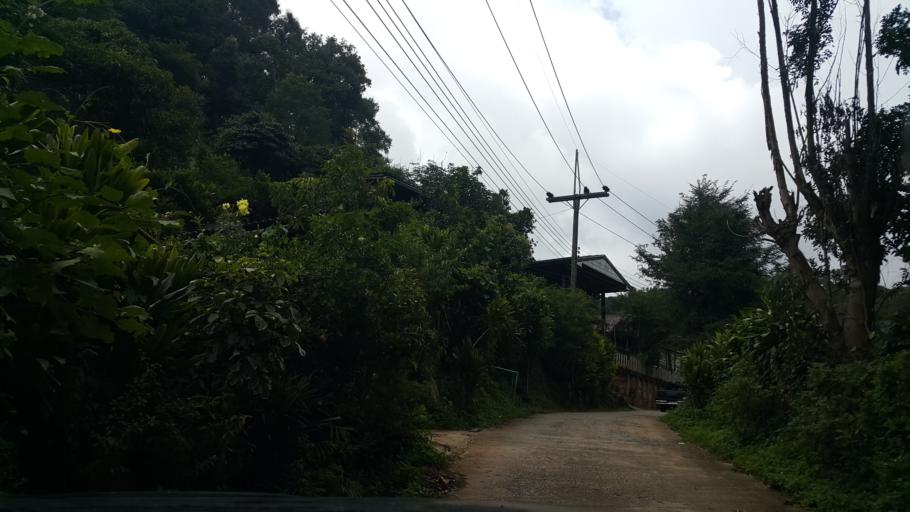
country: TH
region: Lampang
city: Wang Nuea
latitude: 19.0871
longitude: 99.3761
